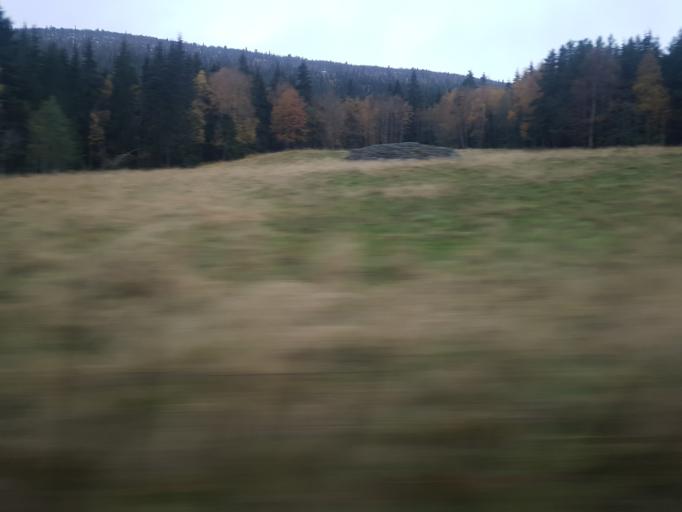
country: NO
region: Oppland
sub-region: Dovre
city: Dovre
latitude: 61.9296
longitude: 9.3170
